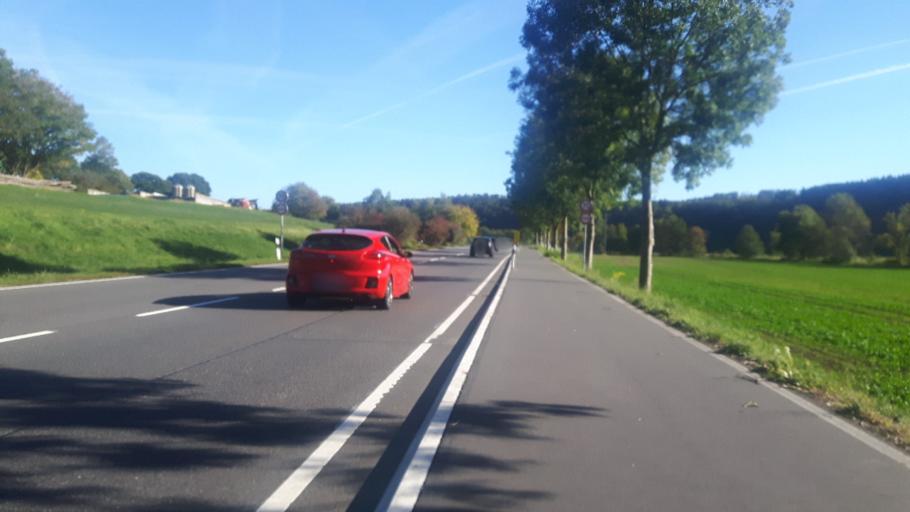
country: DE
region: Rheinland-Pfalz
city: Katzwinkel
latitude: 50.8035
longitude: 7.7990
